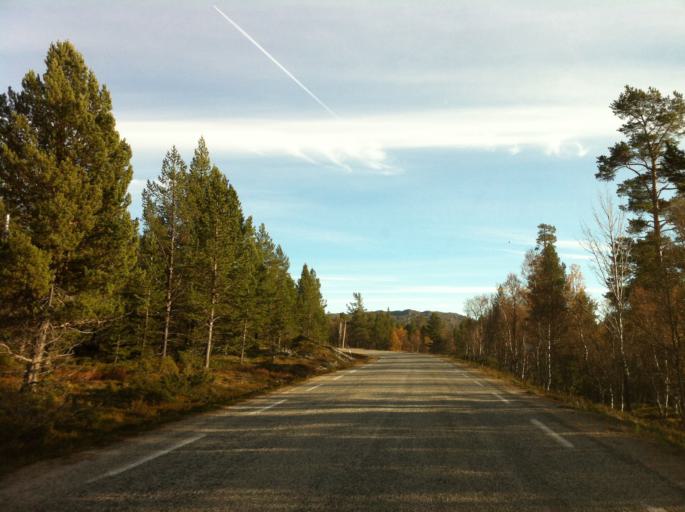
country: NO
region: Hedmark
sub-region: Engerdal
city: Engerdal
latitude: 62.1355
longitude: 11.9806
